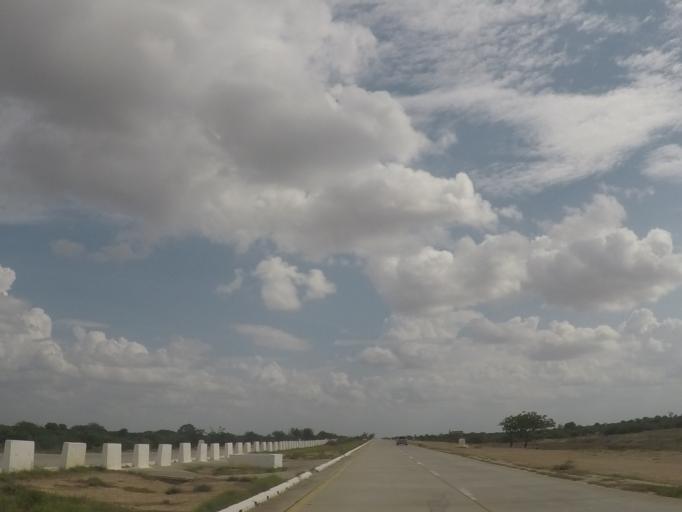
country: MM
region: Mandalay
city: Kyaukse
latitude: 21.4568
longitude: 95.9165
